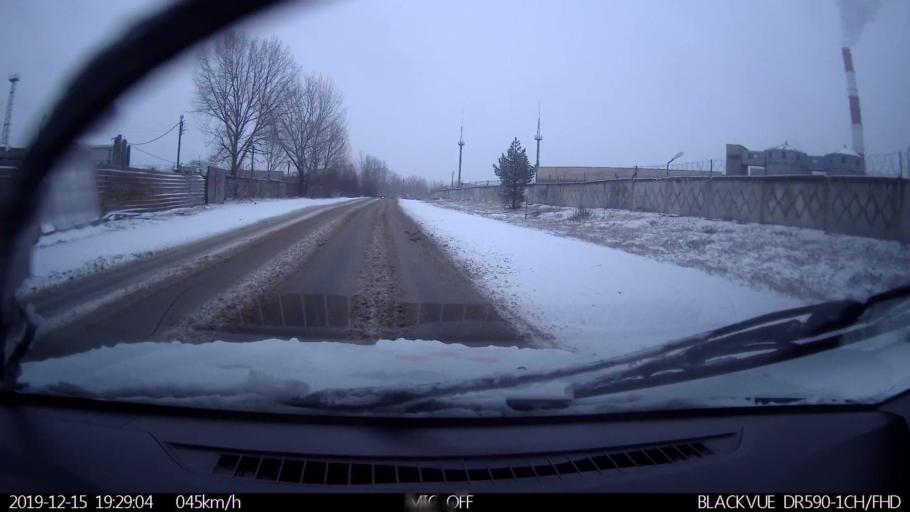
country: RU
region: Nizjnij Novgorod
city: Neklyudovo
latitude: 56.3560
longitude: 43.8929
